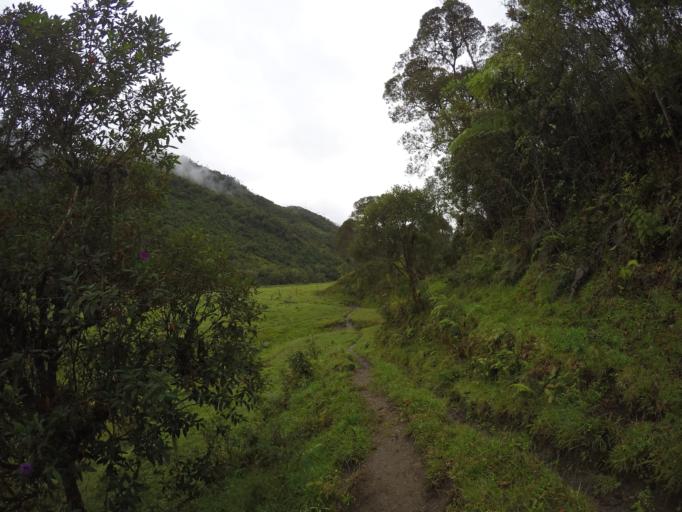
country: CO
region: Tolima
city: Cajamarca
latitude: 4.5148
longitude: -75.3729
